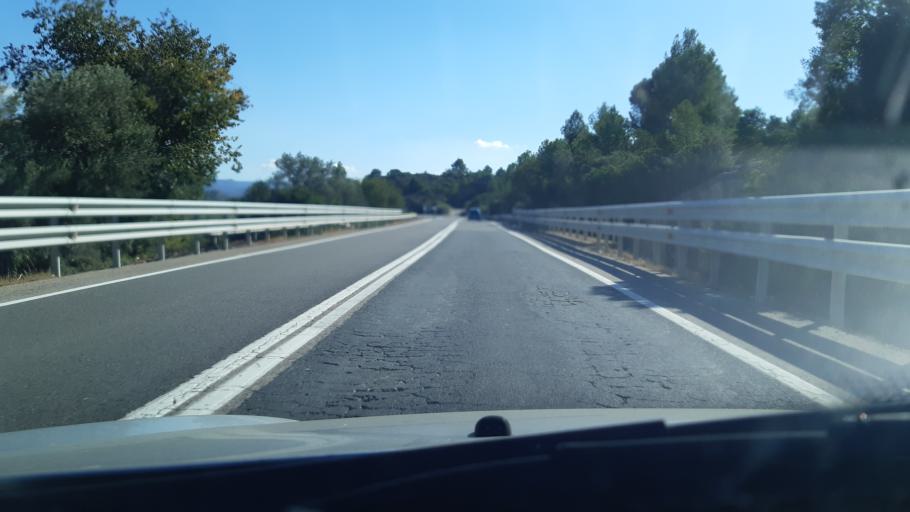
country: ES
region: Catalonia
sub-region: Provincia de Tarragona
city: Tivenys
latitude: 40.9002
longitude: 0.4838
